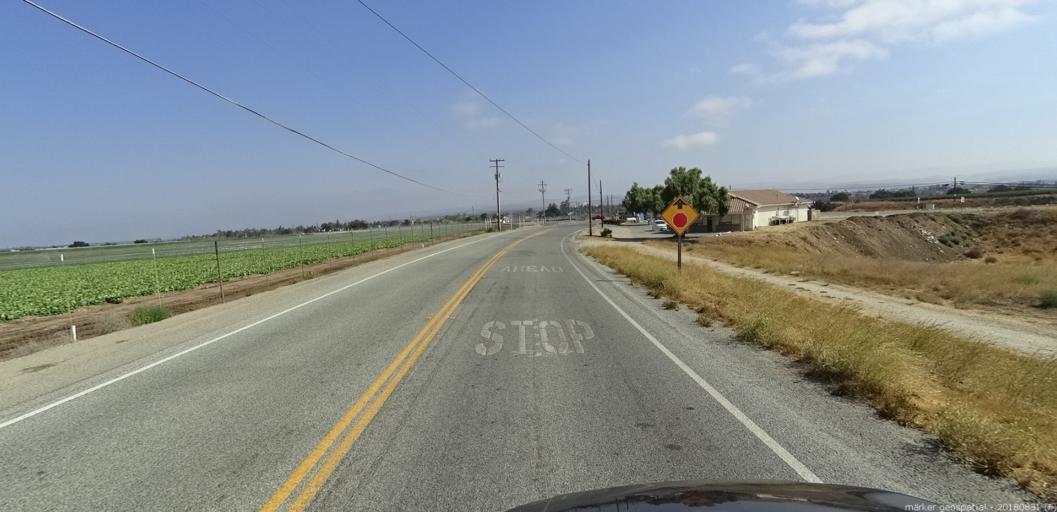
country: US
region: California
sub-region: Monterey County
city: King City
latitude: 36.1915
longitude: -121.1454
